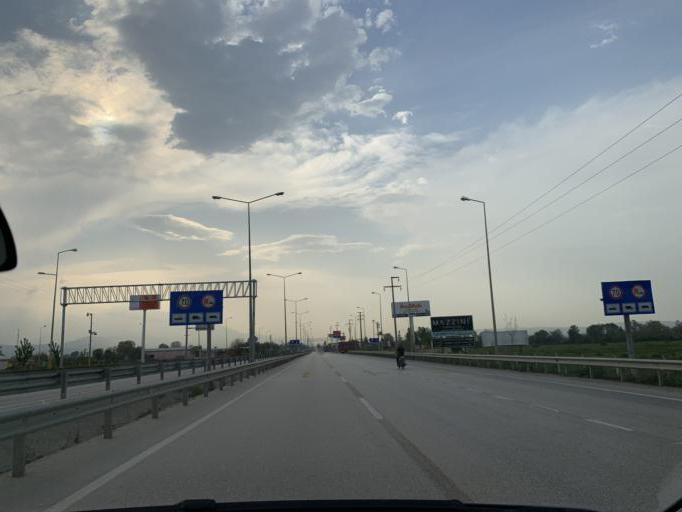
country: TR
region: Bursa
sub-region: Inegoel
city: Inegol
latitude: 40.0658
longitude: 29.5638
